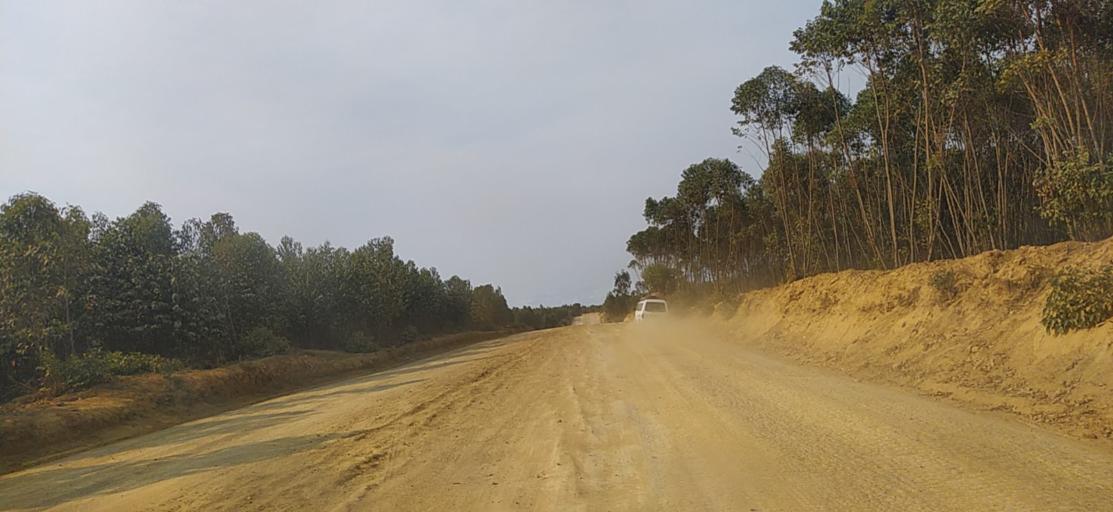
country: MG
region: Alaotra Mangoro
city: Moramanga
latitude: -18.6606
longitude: 48.2739
